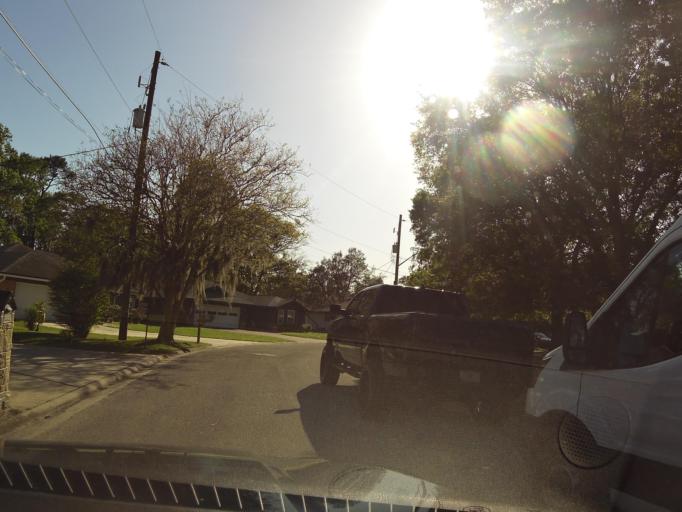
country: US
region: Florida
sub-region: Duval County
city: Jacksonville
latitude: 30.2773
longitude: -81.5826
